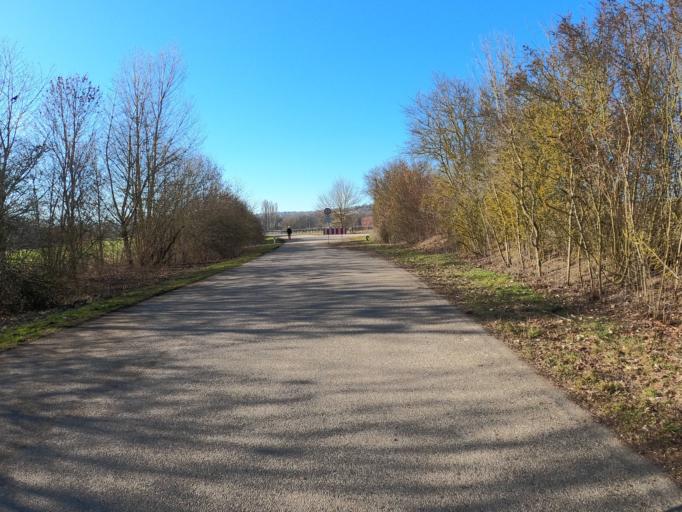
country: DE
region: Bavaria
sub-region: Swabia
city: Neu-Ulm
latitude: 48.4156
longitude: 10.0313
